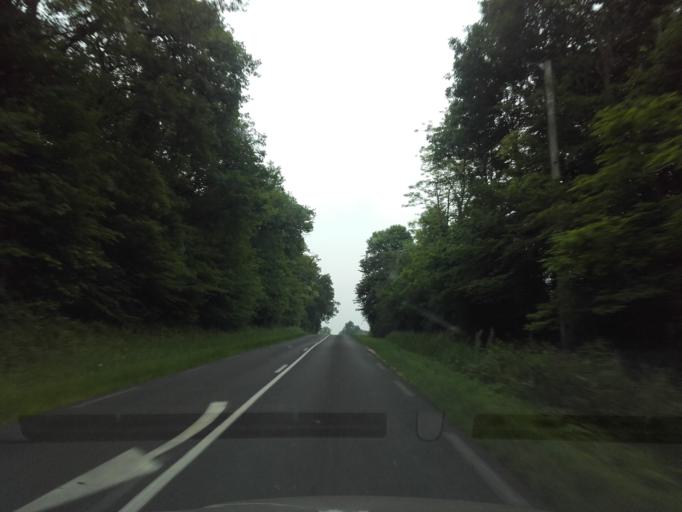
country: FR
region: Centre
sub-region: Departement d'Indre-et-Loire
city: Beaumont-la-Ronce
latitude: 47.6058
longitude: 0.6614
